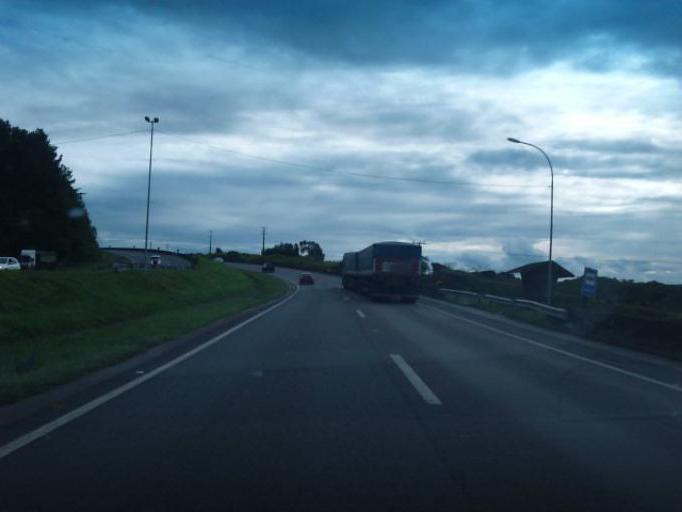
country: BR
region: Parana
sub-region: Campina Grande Do Sul
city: Campina Grande do Sul
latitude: -25.1531
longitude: -48.8607
